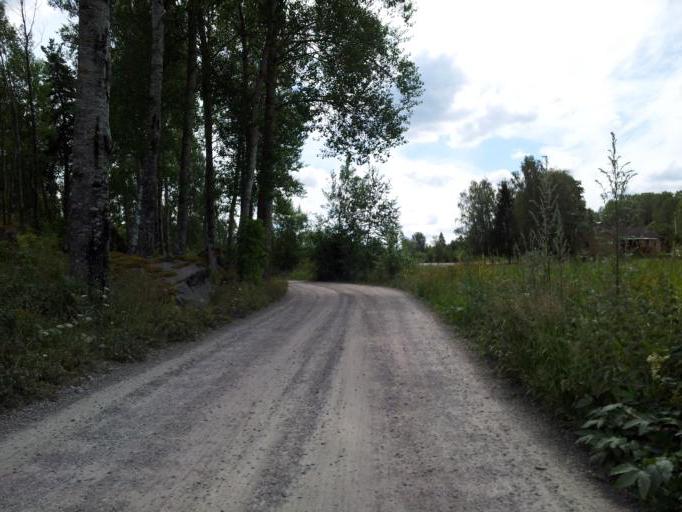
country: SE
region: Stockholm
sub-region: Norrtalje Kommun
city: Nykvarn
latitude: 59.8987
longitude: 18.2442
